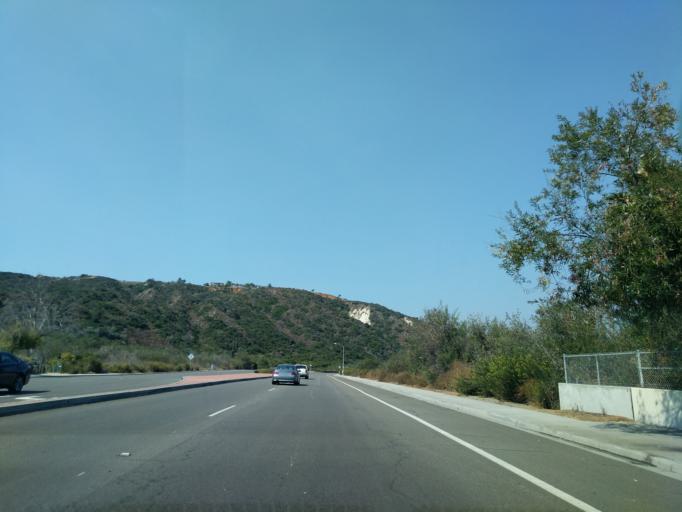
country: US
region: California
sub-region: San Diego County
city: Encinitas
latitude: 33.0854
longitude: -117.2693
